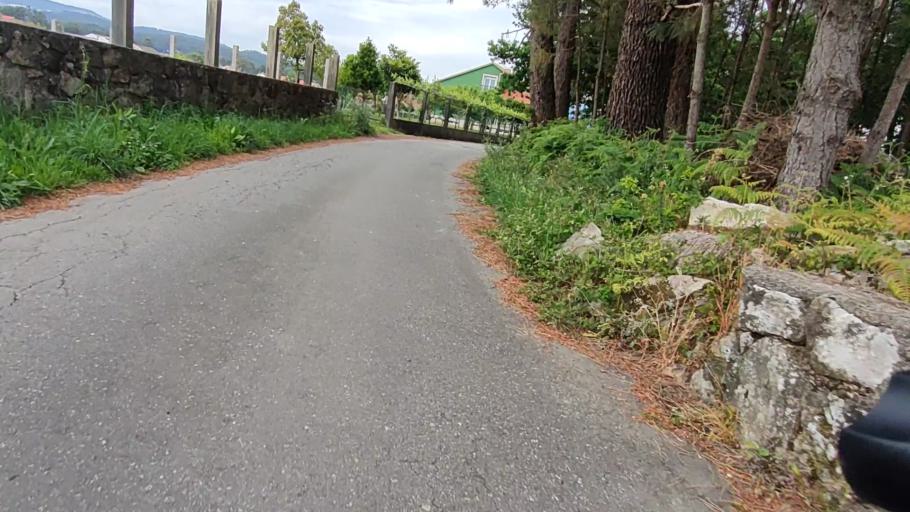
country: ES
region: Galicia
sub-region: Provincia da Coruna
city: Boiro
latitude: 42.6310
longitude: -8.8635
